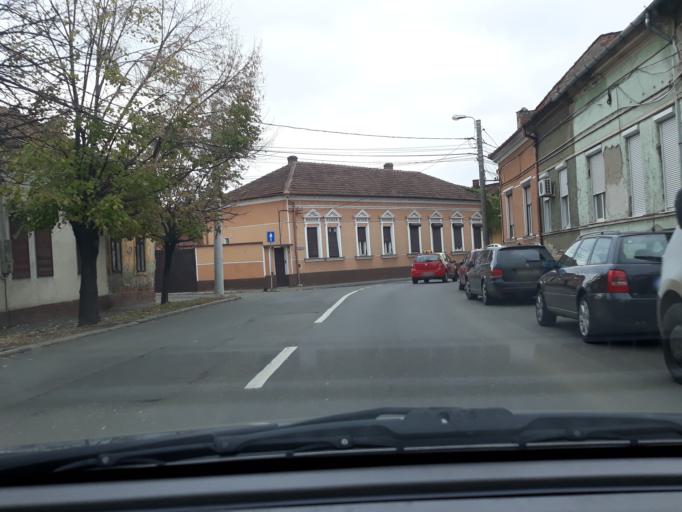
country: RO
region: Bihor
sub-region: Comuna Biharea
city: Oradea
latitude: 47.0631
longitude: 21.9259
